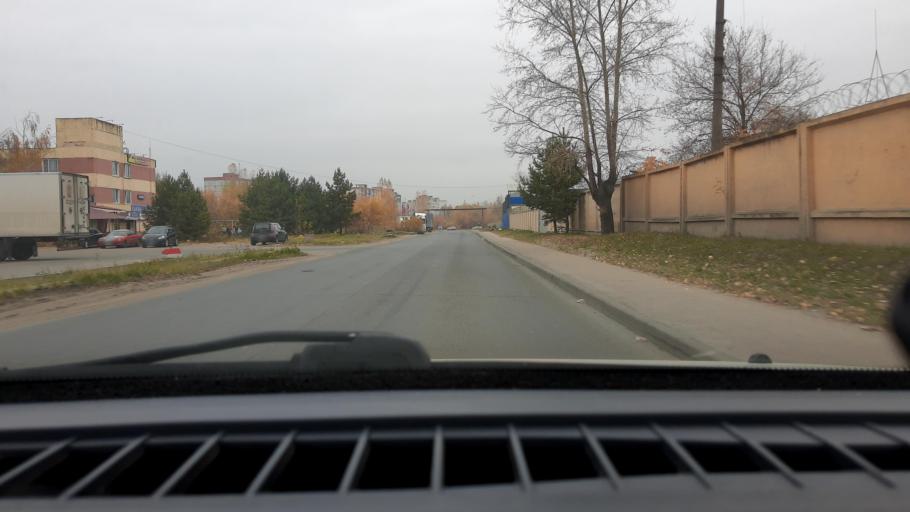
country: RU
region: Nizjnij Novgorod
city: Gorbatovka
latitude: 56.3376
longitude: 43.8065
